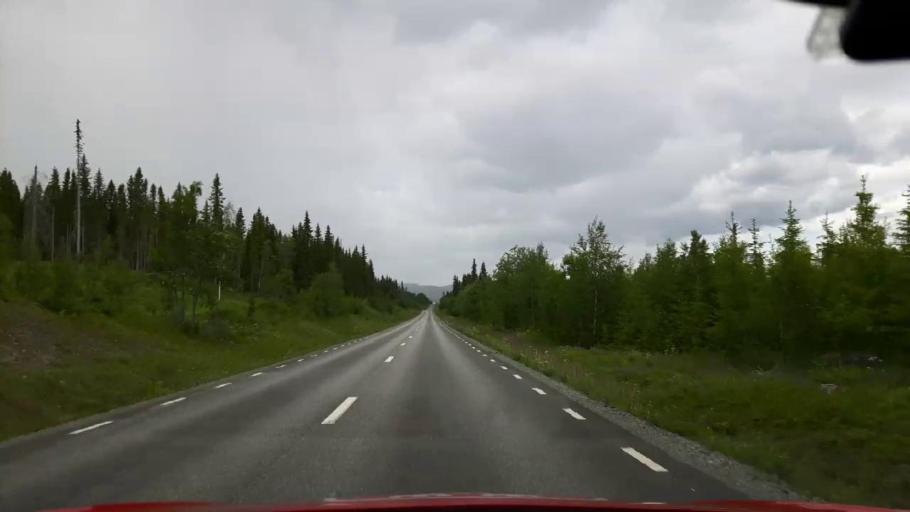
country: SE
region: Jaemtland
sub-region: Krokoms Kommun
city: Krokom
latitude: 63.7089
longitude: 14.3092
